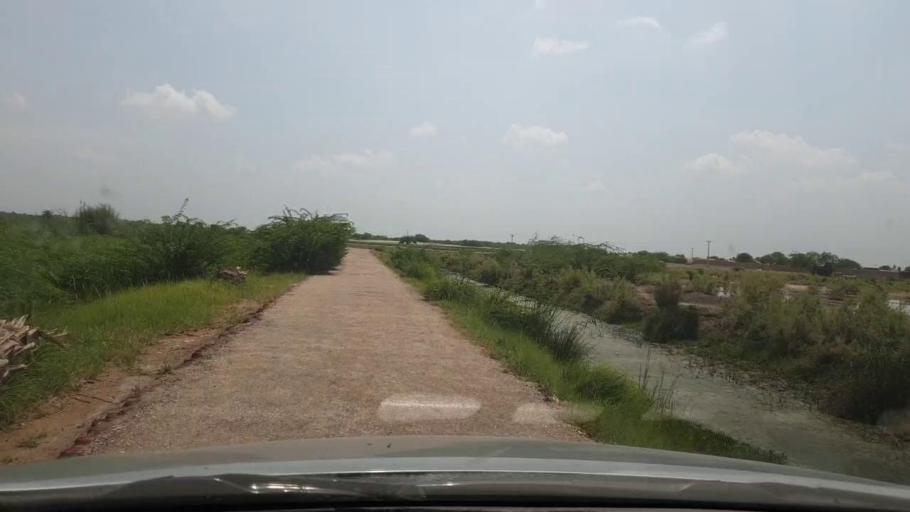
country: PK
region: Sindh
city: Kot Diji
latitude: 27.3890
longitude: 68.7163
